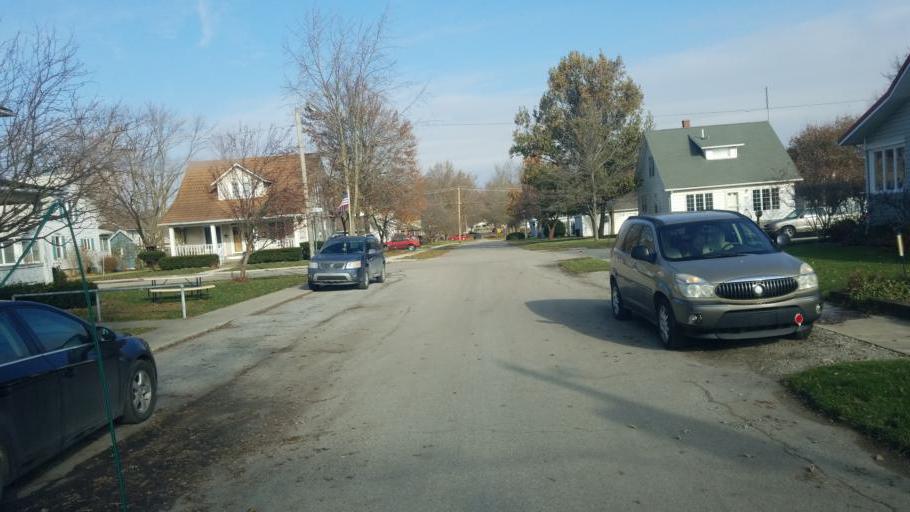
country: US
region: Indiana
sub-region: Adams County
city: Berne
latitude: 40.6611
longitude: -84.9527
